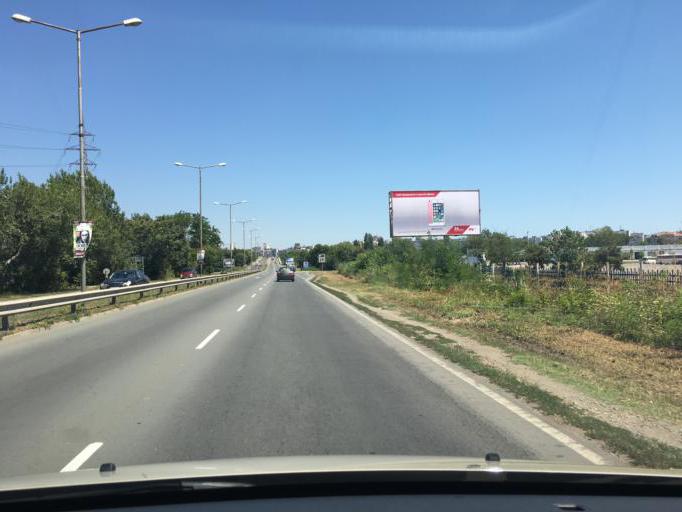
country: BG
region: Burgas
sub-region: Obshtina Burgas
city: Burgas
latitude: 42.4947
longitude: 27.4518
